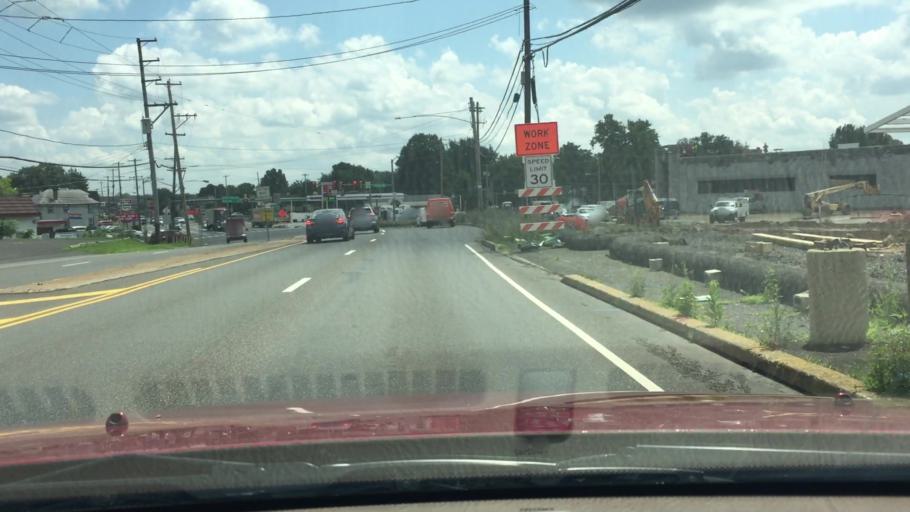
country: US
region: Pennsylvania
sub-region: Montgomery County
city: Horsham
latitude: 40.1727
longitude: -75.1281
